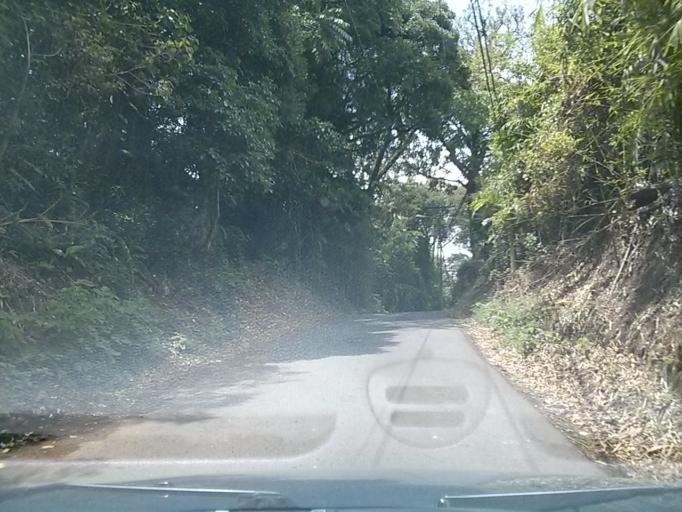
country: CR
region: Heredia
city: Santo Domingo
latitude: 10.0740
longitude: -84.1066
